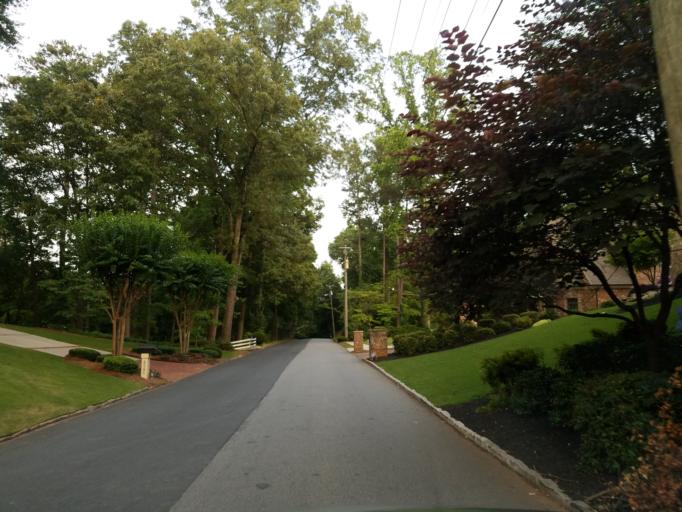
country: US
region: Georgia
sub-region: Fulton County
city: Sandy Springs
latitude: 33.8792
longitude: -84.3906
